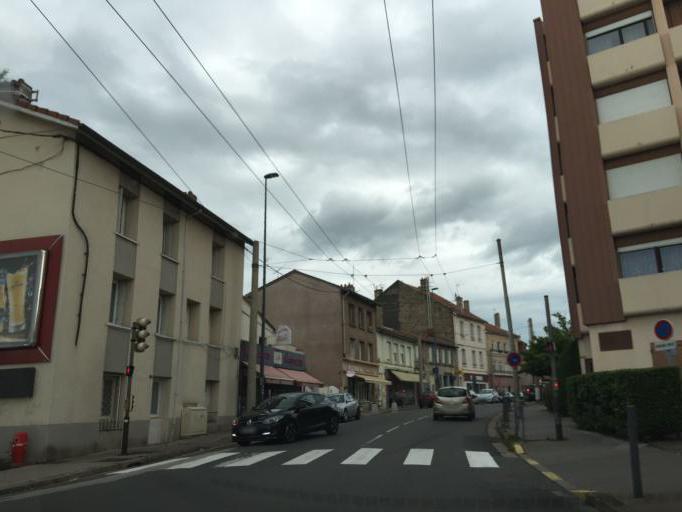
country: FR
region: Rhone-Alpes
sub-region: Departement de la Loire
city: Saint-Etienne
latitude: 45.4416
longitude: 4.4146
